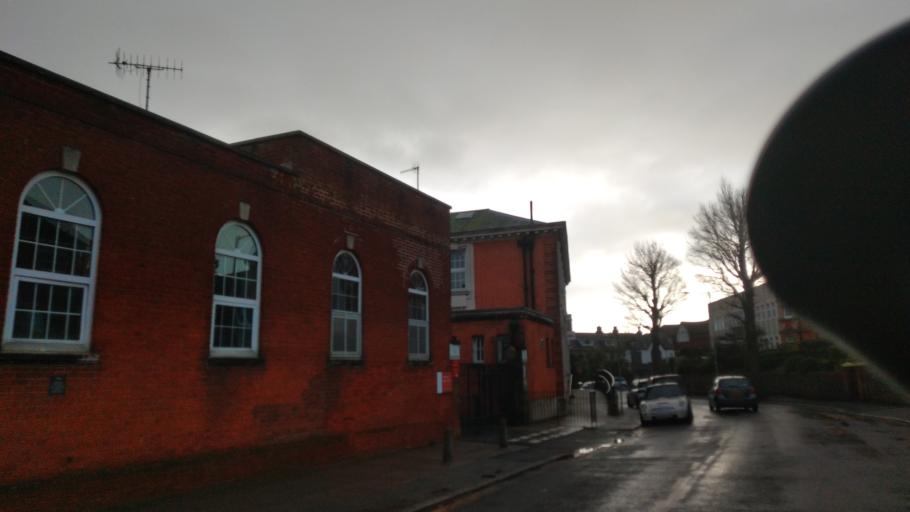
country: GB
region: England
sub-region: East Sussex
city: Eastbourne
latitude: 50.7694
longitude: 0.2782
